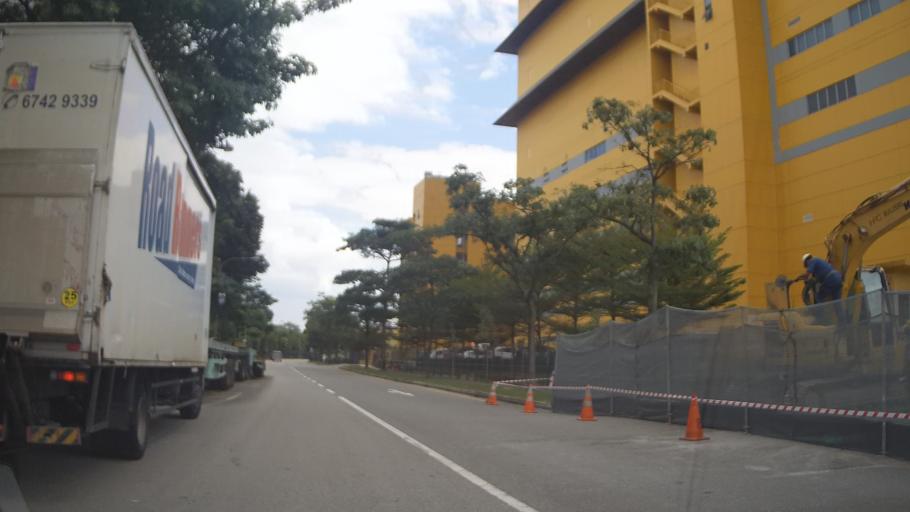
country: SG
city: Singapore
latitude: 1.3054
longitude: 103.7580
